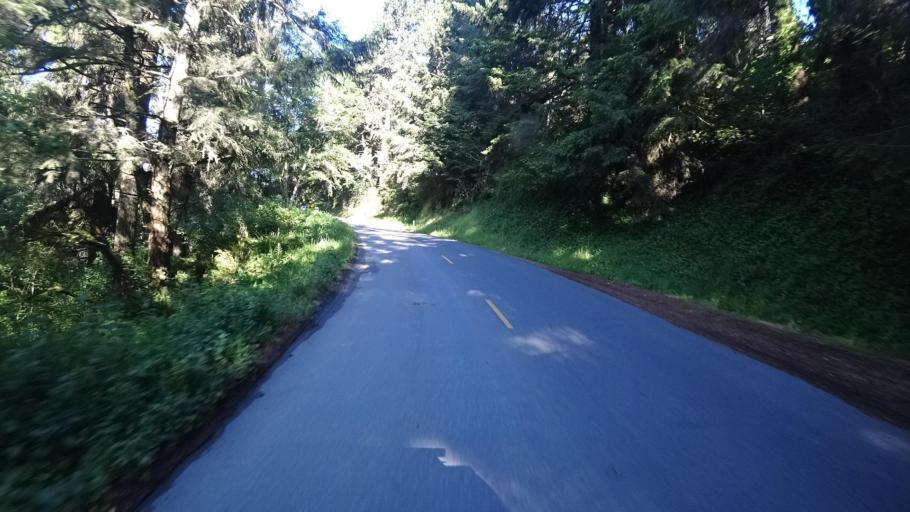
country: US
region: California
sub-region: Humboldt County
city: Westhaven-Moonstone
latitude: 41.0346
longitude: -124.1132
